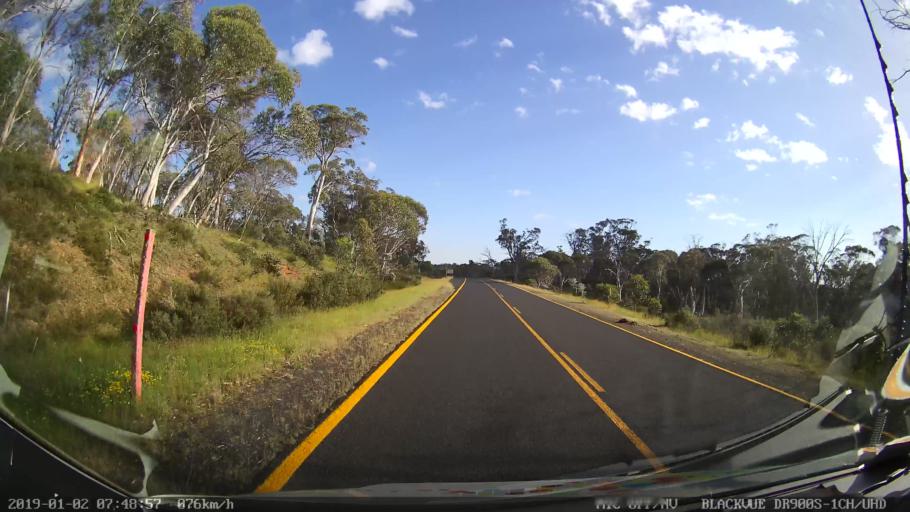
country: AU
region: New South Wales
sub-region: Tumut Shire
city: Tumut
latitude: -35.7472
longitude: 148.5207
